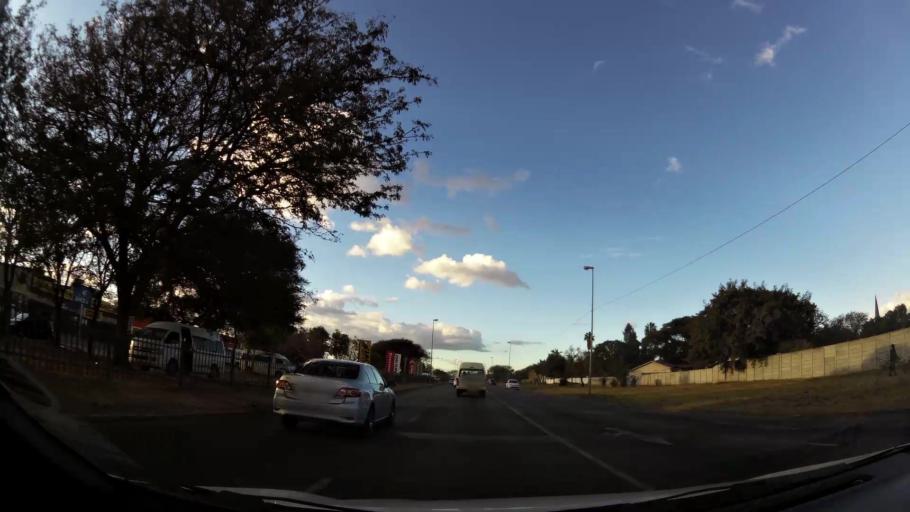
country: ZA
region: Limpopo
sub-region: Capricorn District Municipality
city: Polokwane
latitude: -23.8921
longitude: 29.4527
